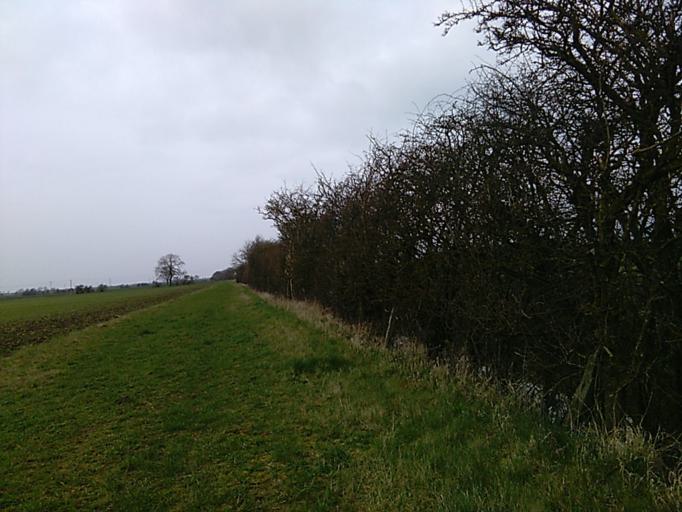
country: GB
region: England
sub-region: Nottinghamshire
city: Bingham
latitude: 52.9172
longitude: -0.9348
